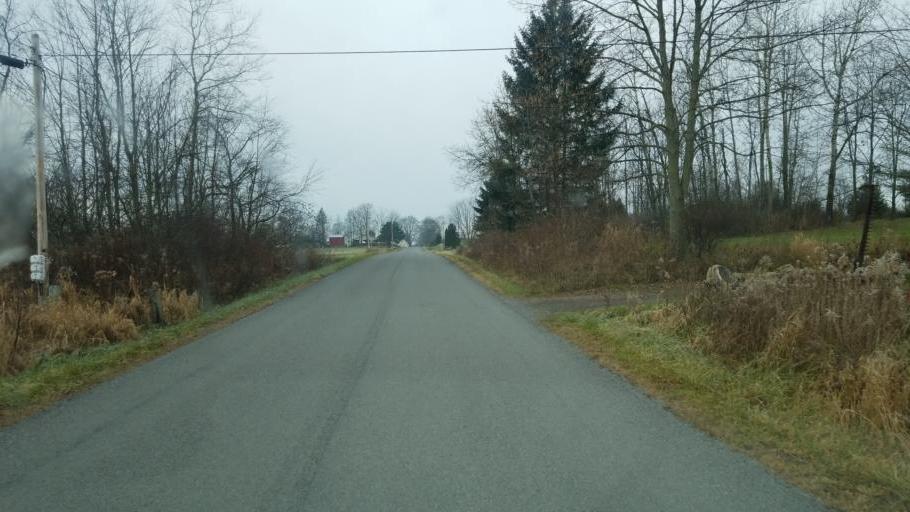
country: US
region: Pennsylvania
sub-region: Crawford County
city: Cochranton
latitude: 41.5088
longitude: -80.0847
